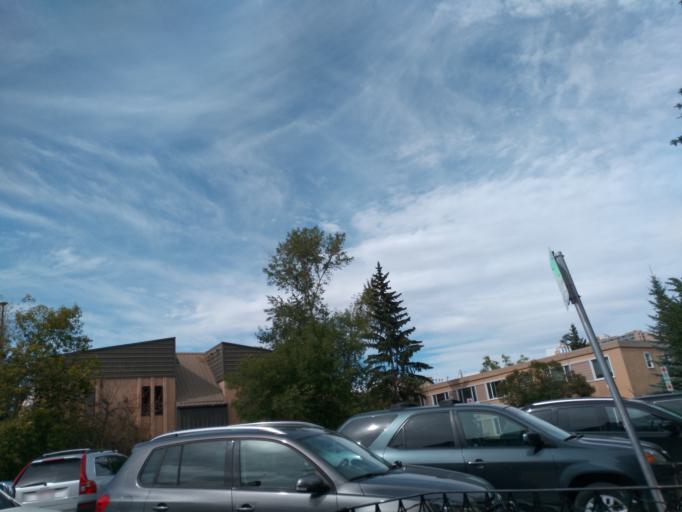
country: CA
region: Alberta
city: Calgary
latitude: 51.0582
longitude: -114.1357
